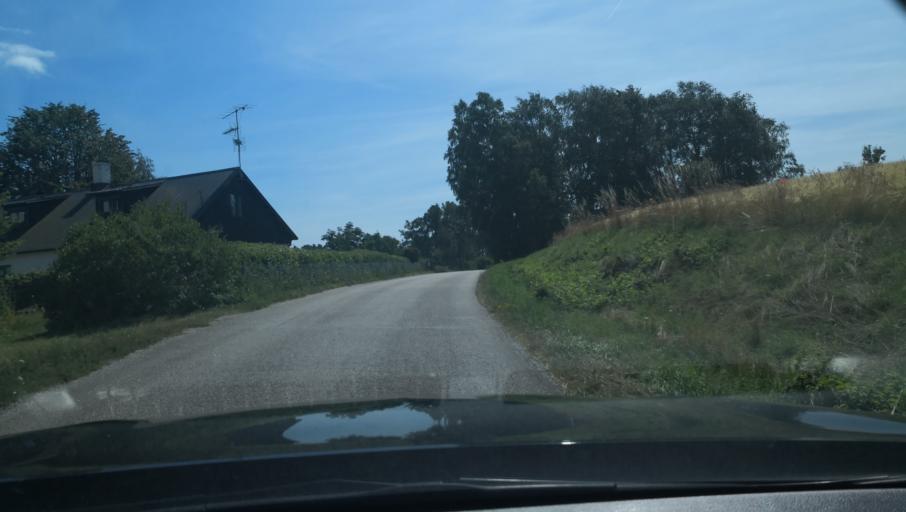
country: SE
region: Skane
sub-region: Ystads Kommun
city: Kopingebro
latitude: 55.3901
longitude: 14.1417
